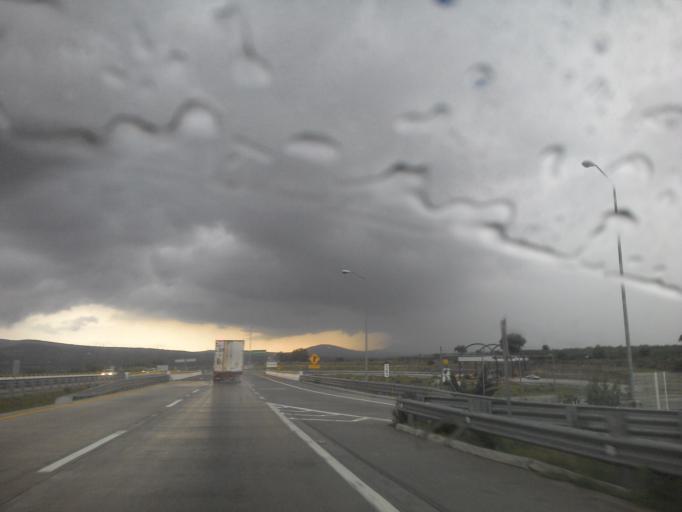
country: MX
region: Morelos
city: Nopaltepec
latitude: 19.8343
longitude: -98.7010
